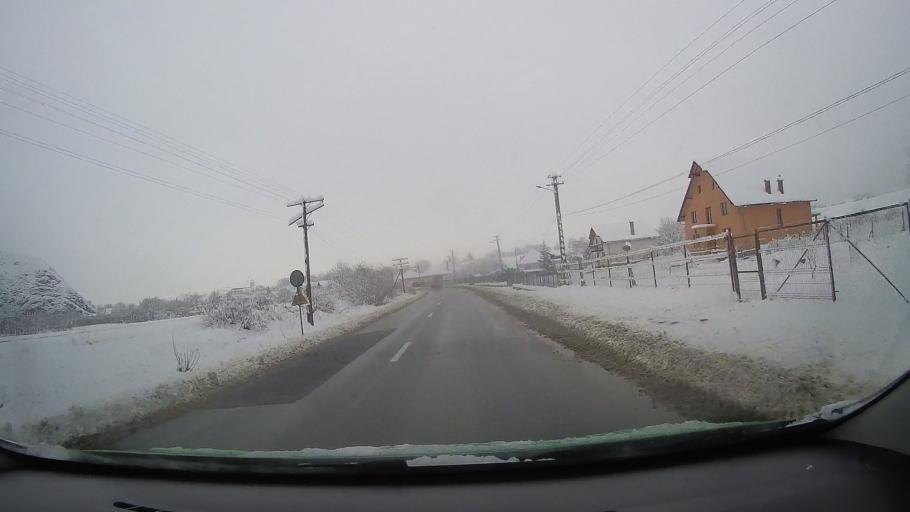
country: RO
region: Sibiu
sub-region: Comuna Orlat
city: Orlat
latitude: 45.7559
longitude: 23.9578
